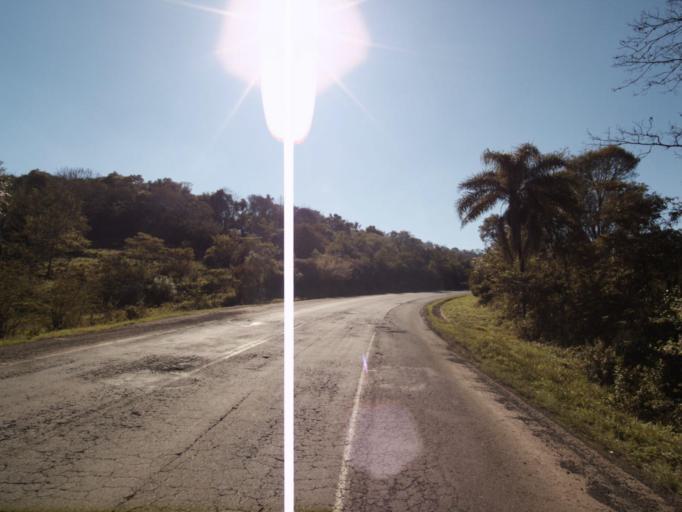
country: BR
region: Rio Grande do Sul
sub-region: Frederico Westphalen
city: Frederico Westphalen
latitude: -27.0678
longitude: -53.2281
